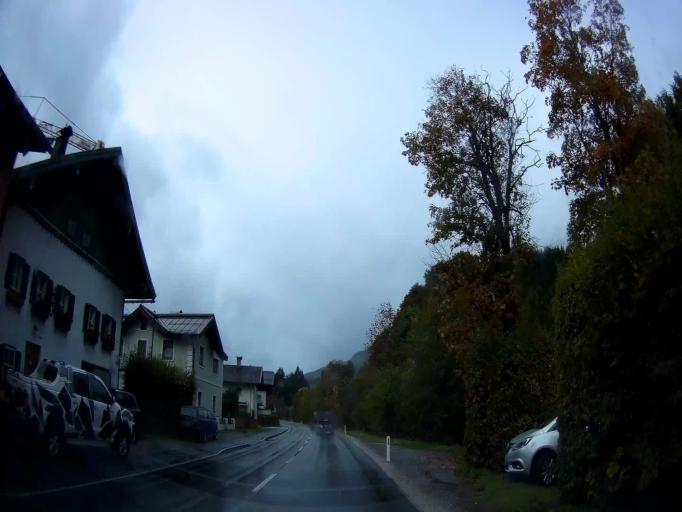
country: AT
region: Salzburg
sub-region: Politischer Bezirk Zell am See
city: Leogang
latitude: 47.4393
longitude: 12.7520
